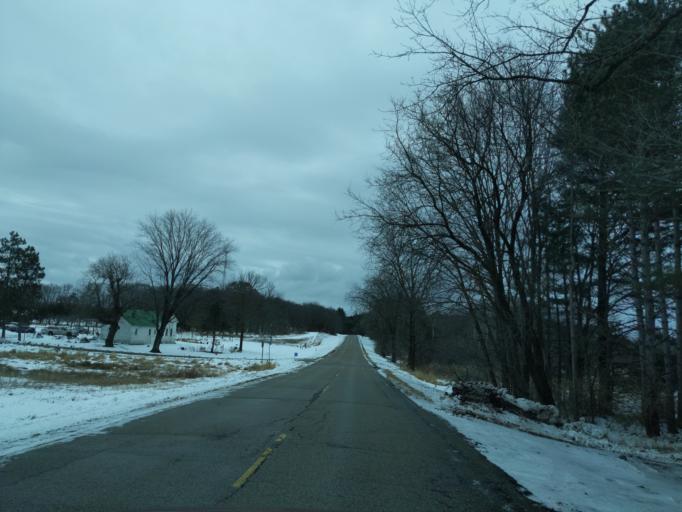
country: US
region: Wisconsin
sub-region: Marquette County
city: Montello
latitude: 43.9151
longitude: -89.3407
